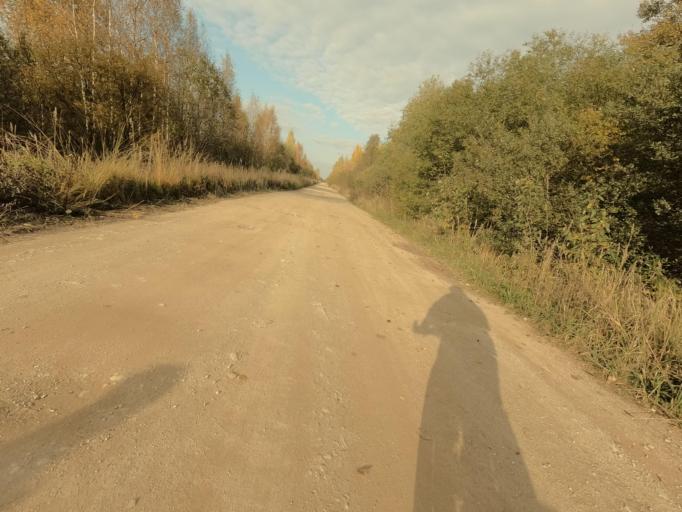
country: RU
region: Novgorod
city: Volkhovskiy
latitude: 58.9035
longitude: 31.0349
